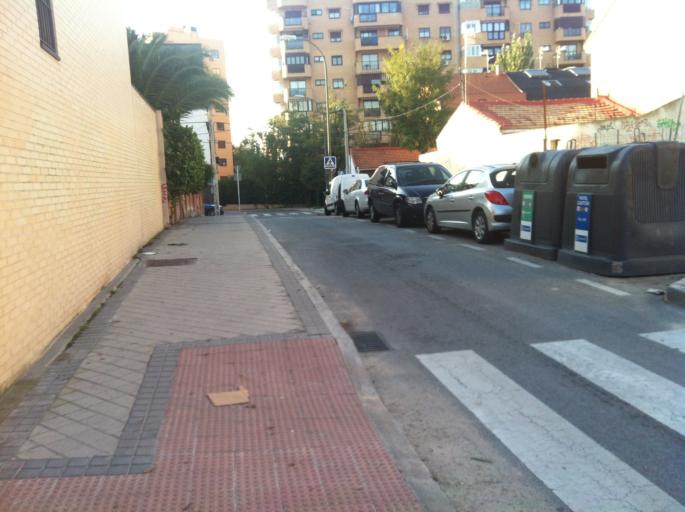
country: ES
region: Madrid
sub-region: Provincia de Madrid
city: Tetuan de las Victorias
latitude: 40.4661
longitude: -3.7137
